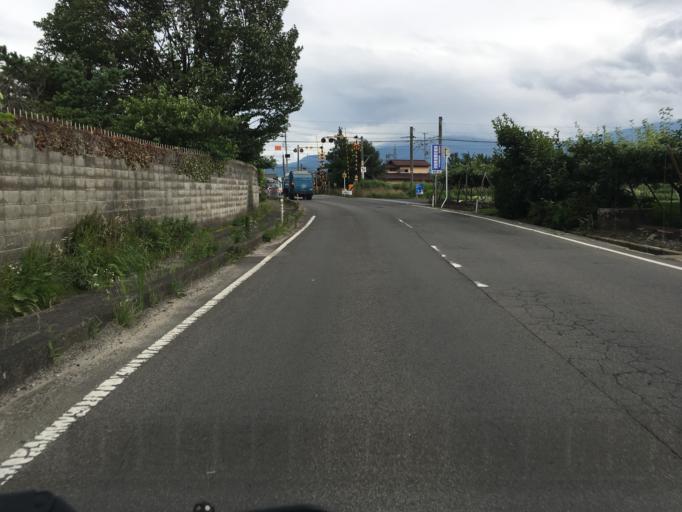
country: JP
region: Fukushima
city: Fukushima-shi
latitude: 37.7702
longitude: 140.4025
